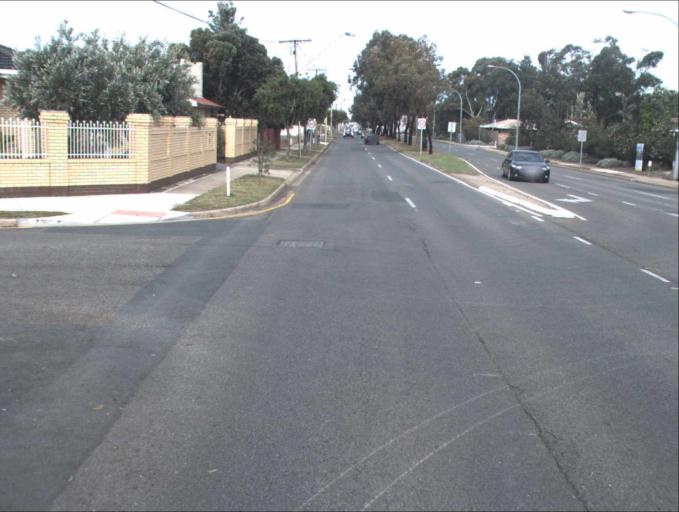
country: AU
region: South Australia
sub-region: Charles Sturt
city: Royal Park
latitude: -34.8741
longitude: 138.5036
